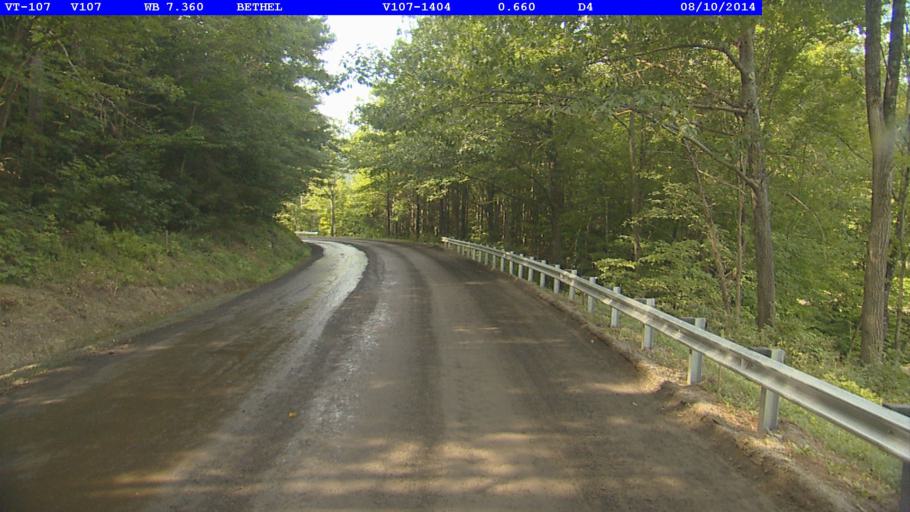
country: US
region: Vermont
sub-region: Orange County
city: Randolph
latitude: 43.8044
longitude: -72.6651
